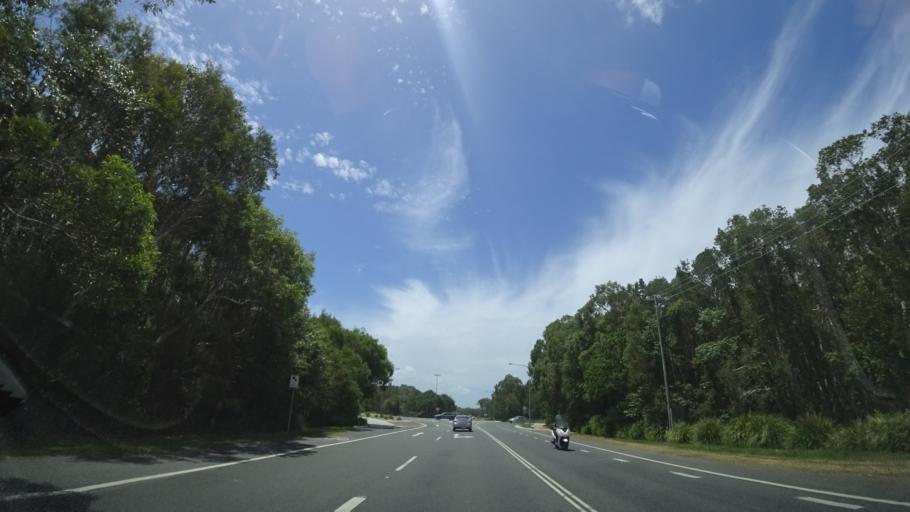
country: AU
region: Queensland
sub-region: Sunshine Coast
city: Coolum Beach
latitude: -26.5701
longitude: 153.0933
